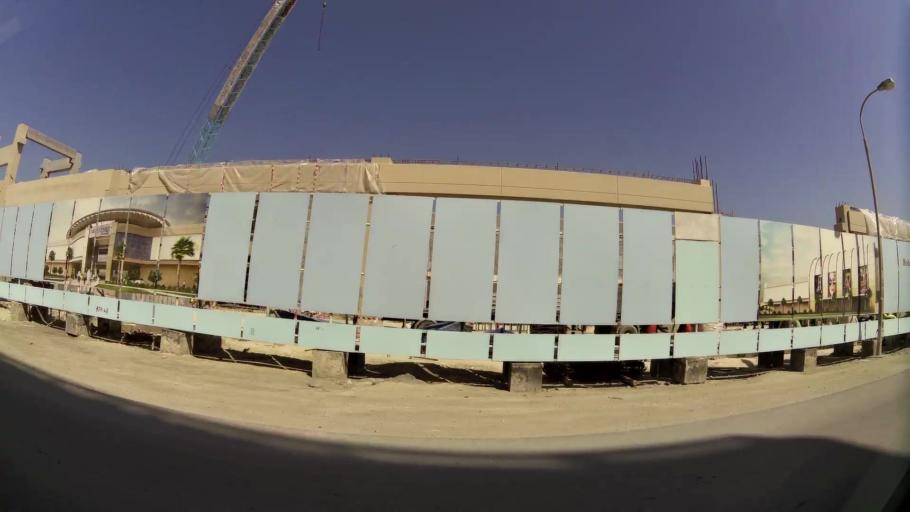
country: BH
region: Manama
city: Manama
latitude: 26.2153
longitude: 50.5990
